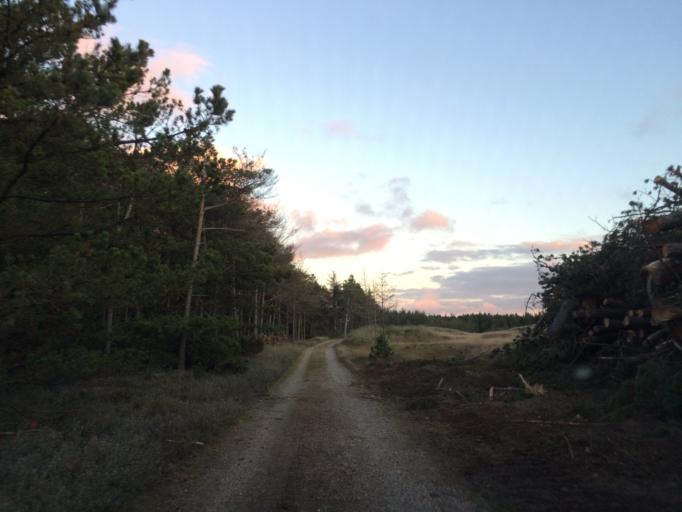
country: DK
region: Central Jutland
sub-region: Holstebro Kommune
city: Ulfborg
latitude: 56.2999
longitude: 8.1460
